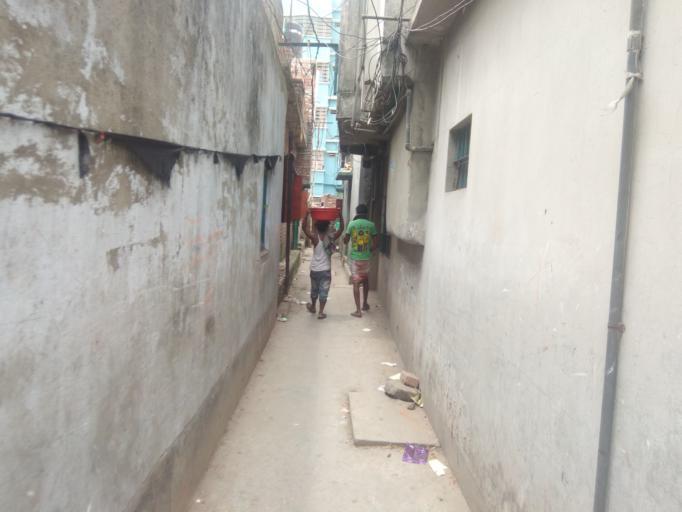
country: BD
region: Dhaka
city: Azimpur
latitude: 23.7094
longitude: 90.3773
